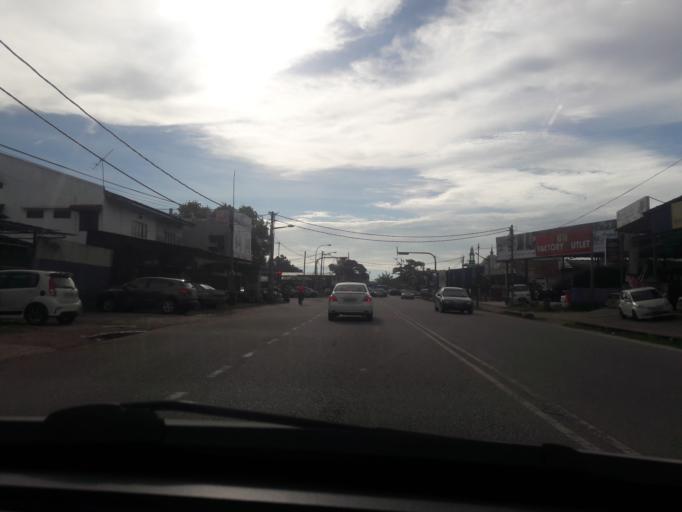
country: MY
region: Kedah
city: Sungai Petani
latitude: 5.6346
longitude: 100.5028
